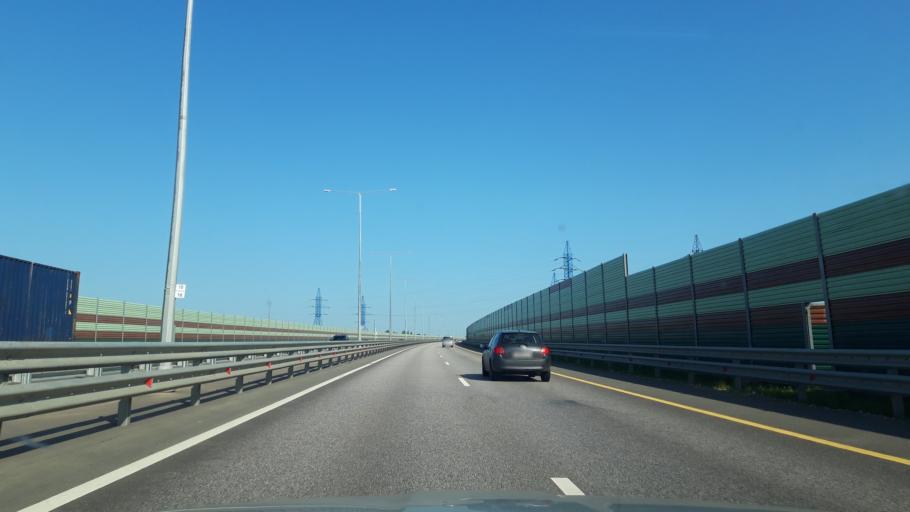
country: RU
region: Moskovskaya
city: Klin
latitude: 56.3112
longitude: 36.6510
